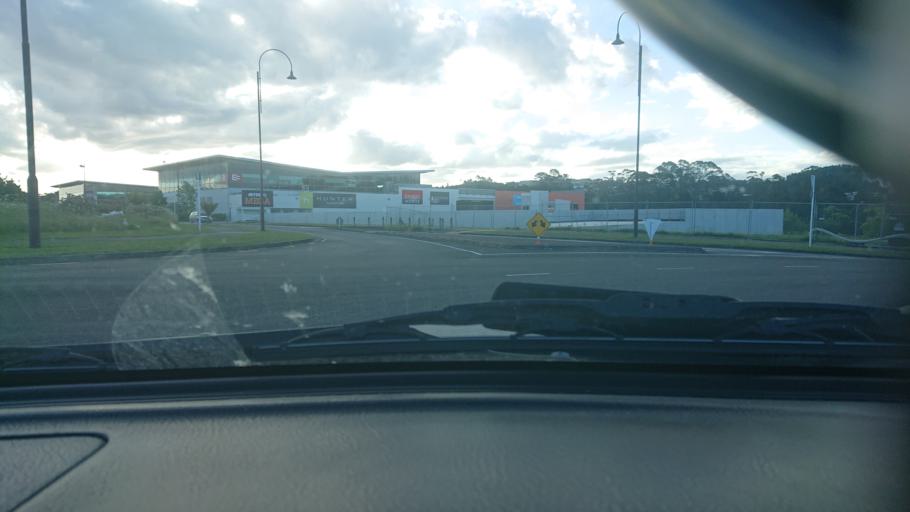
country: NZ
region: Auckland
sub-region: Auckland
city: Rothesay Bay
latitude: -36.7223
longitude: 174.7087
